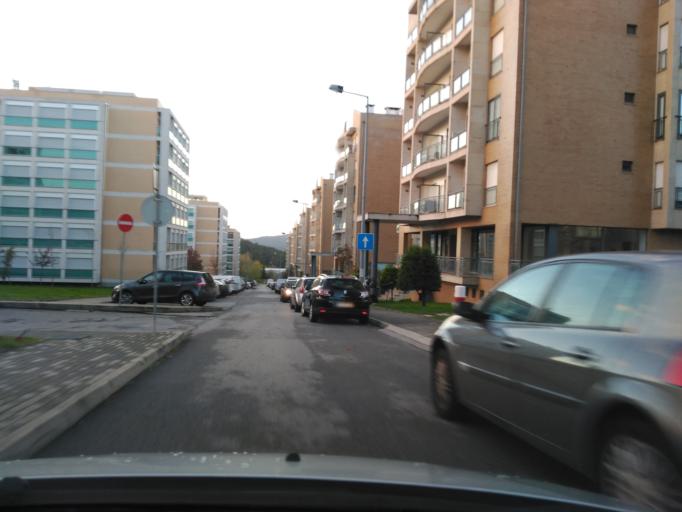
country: PT
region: Braga
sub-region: Braga
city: Braga
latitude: 41.5314
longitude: -8.4113
